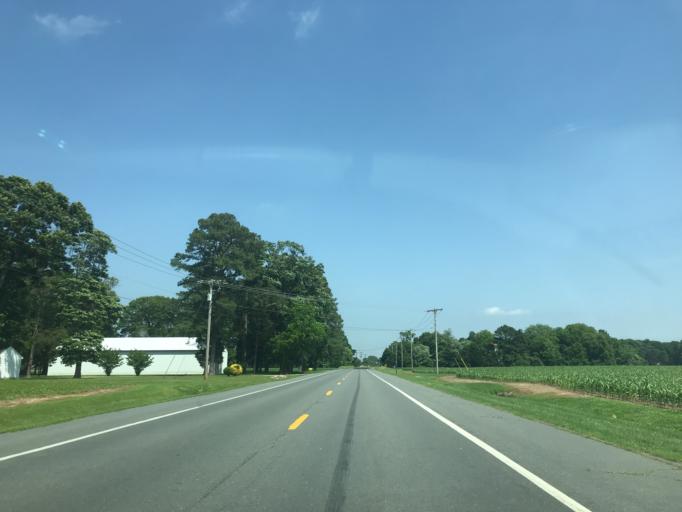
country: US
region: Maryland
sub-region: Dorchester County
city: Hurlock
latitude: 38.5916
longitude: -75.8818
